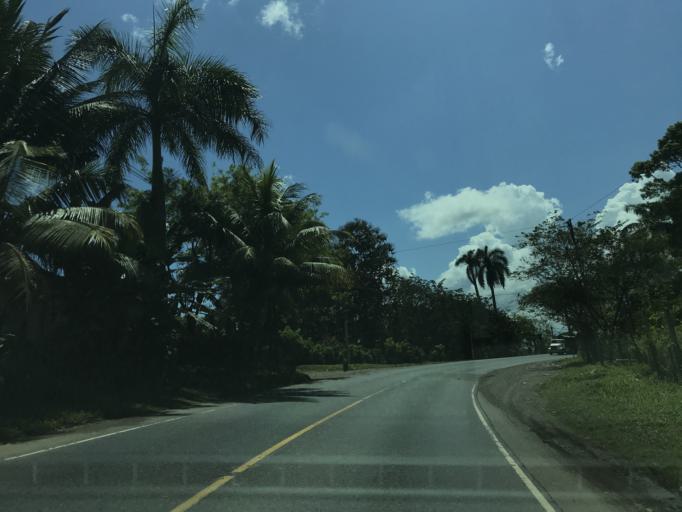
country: GT
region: Izabal
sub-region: Municipio de Puerto Barrios
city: Puerto Barrios
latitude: 15.6625
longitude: -88.5504
